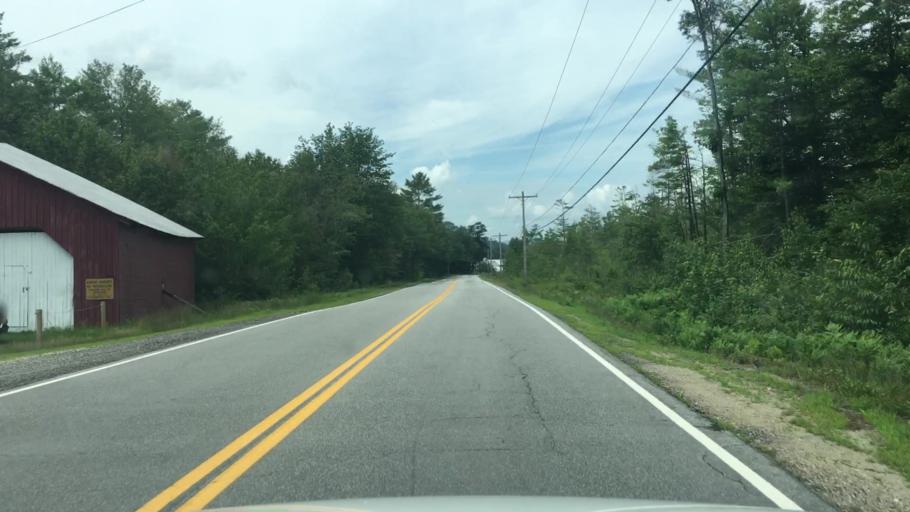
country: US
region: New Hampshire
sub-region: Grafton County
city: Rumney
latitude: 43.7790
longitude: -71.7539
